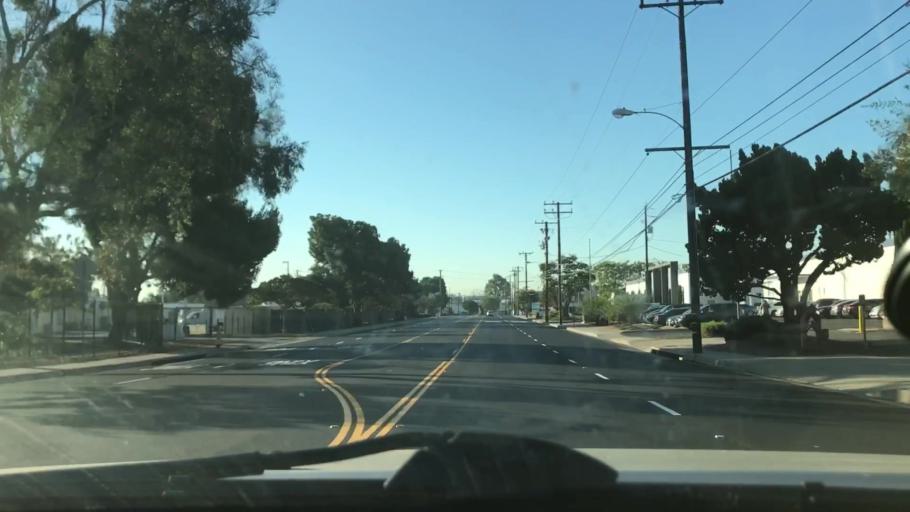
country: US
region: California
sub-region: Los Angeles County
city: Del Aire
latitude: 33.9126
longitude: -118.3832
